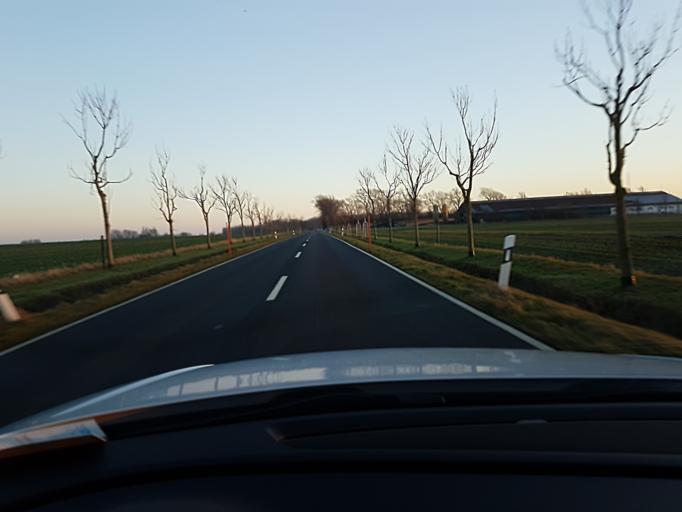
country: DE
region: Mecklenburg-Vorpommern
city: Wiek
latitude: 54.6053
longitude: 13.2856
